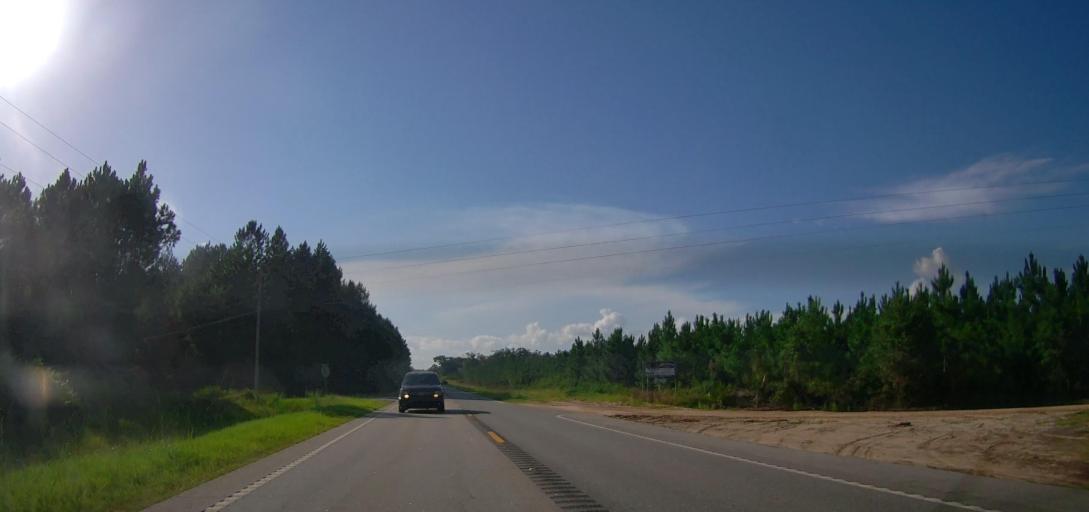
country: US
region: Georgia
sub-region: Coffee County
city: Nicholls
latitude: 31.4261
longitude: -82.6987
